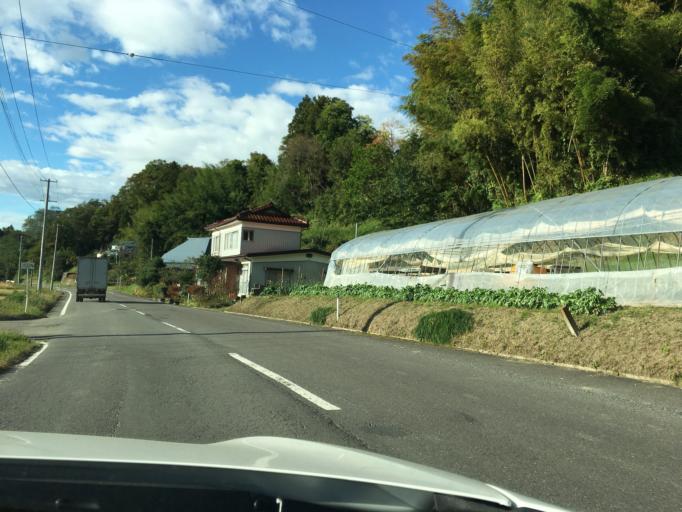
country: JP
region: Fukushima
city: Ishikawa
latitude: 37.2315
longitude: 140.4514
